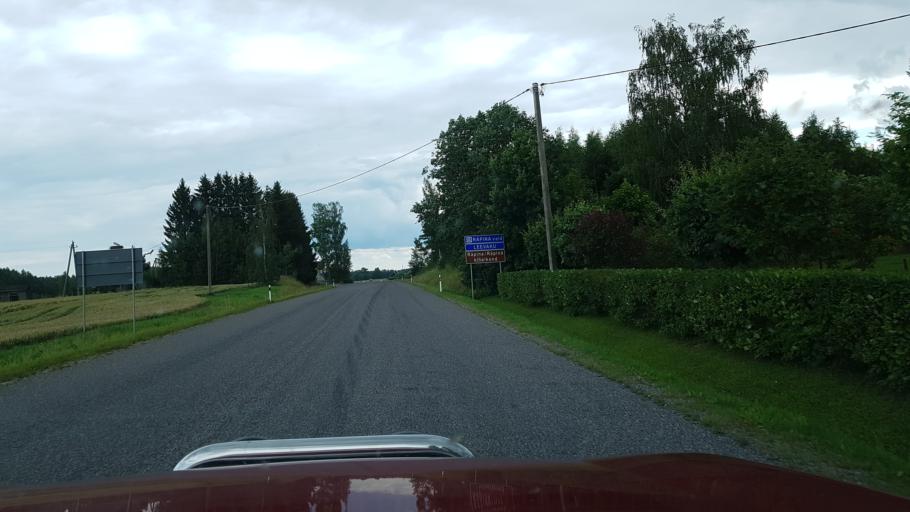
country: EE
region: Polvamaa
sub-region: Raepina vald
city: Rapina
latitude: 58.1185
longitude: 27.2917
